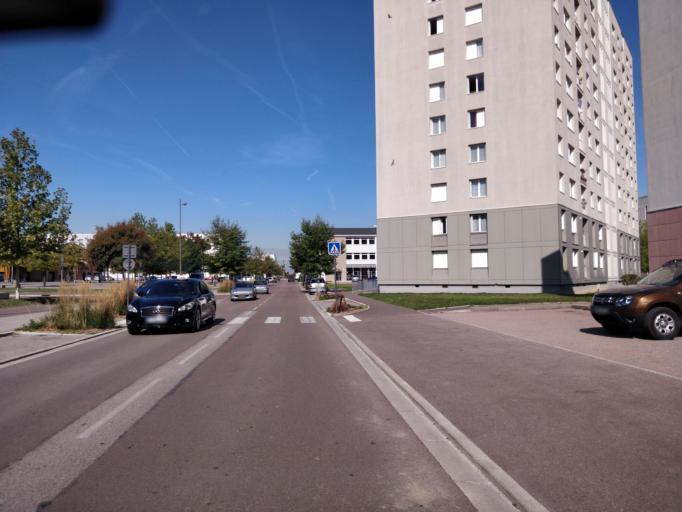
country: FR
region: Champagne-Ardenne
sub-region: Departement de l'Aube
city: Rosieres-pres-Troyes
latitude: 48.2707
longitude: 4.0848
